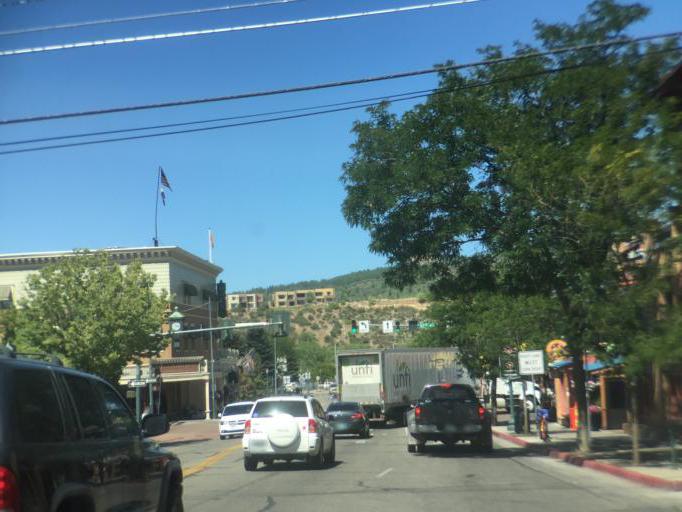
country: US
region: Colorado
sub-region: La Plata County
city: Durango
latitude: 37.2700
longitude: -107.8809
